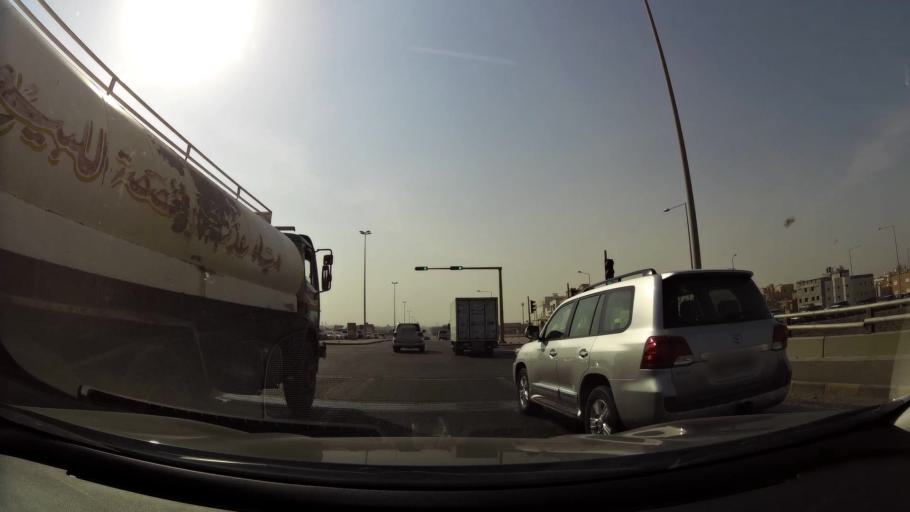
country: KW
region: Al Ahmadi
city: Al Fintas
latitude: 29.1607
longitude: 48.1104
